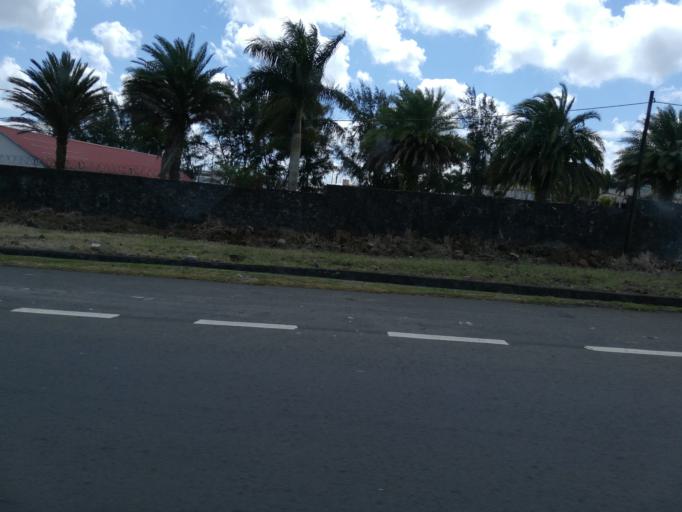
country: MU
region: Plaines Wilhems
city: Quatre Bornes
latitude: -20.2786
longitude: 57.5052
